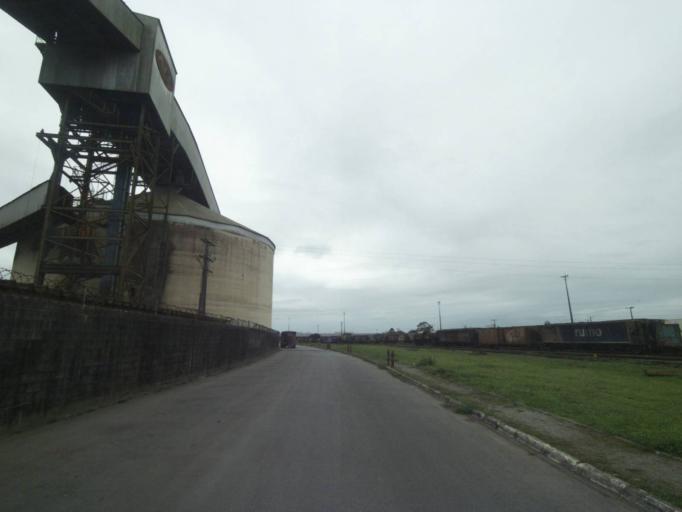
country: BR
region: Parana
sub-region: Paranagua
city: Paranagua
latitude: -25.5417
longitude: -48.5417
